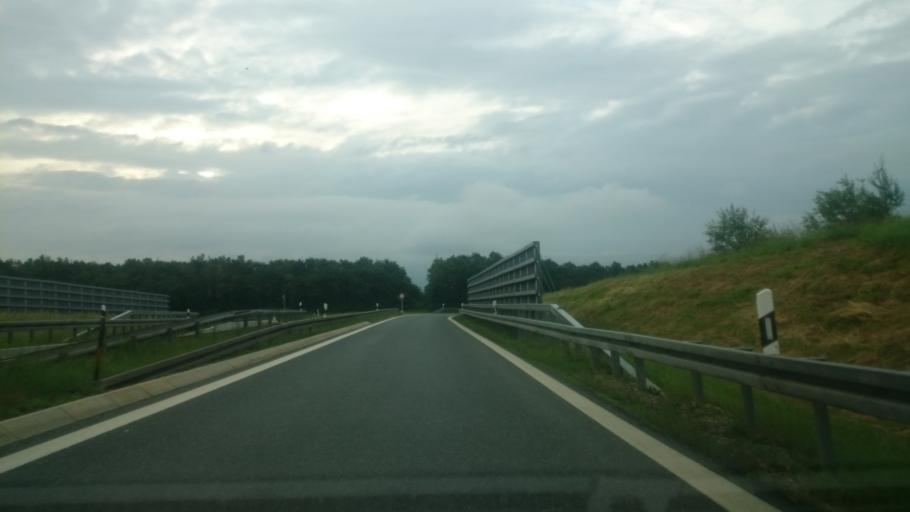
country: DE
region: Bavaria
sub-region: Regierungsbezirk Mittelfranken
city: Allersberg
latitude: 49.2515
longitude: 11.2135
